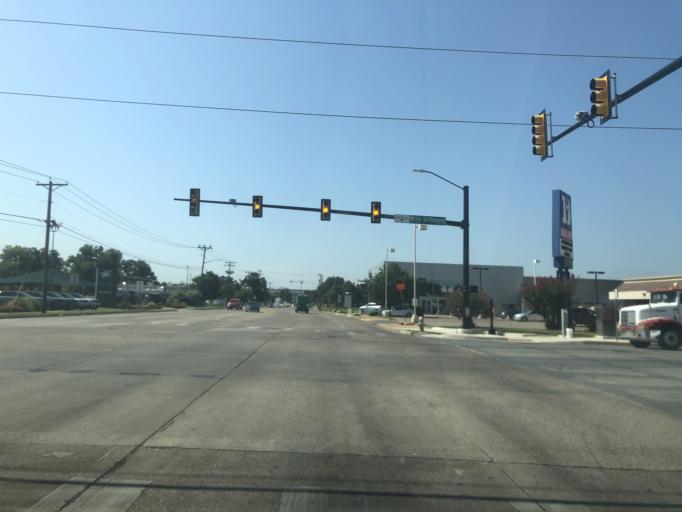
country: US
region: Texas
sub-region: Tarrant County
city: River Oaks
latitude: 32.7595
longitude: -97.3612
